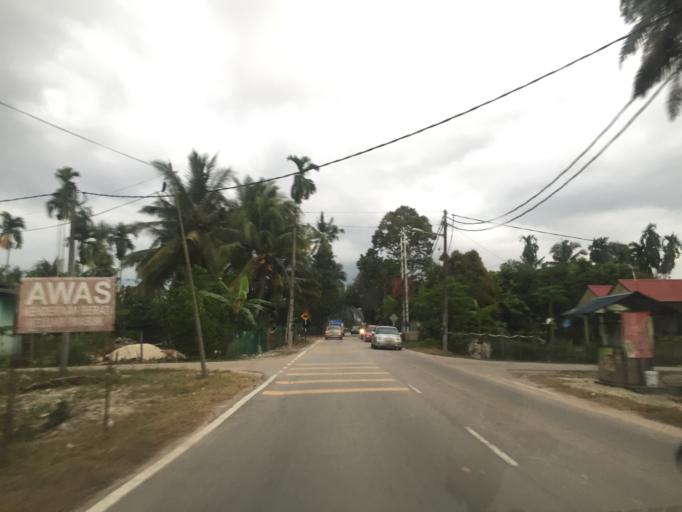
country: MY
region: Penang
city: Tasek Glugor
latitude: 5.5416
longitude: 100.5275
